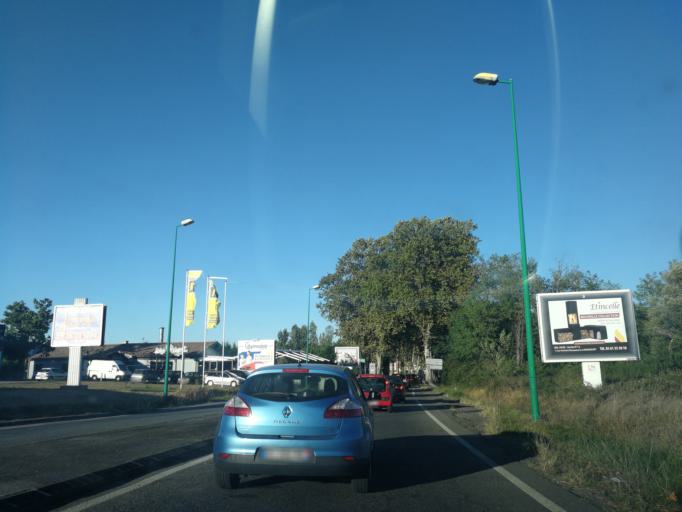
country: FR
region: Midi-Pyrenees
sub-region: Departement de la Haute-Garonne
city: Montrabe
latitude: 43.6386
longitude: 1.5013
